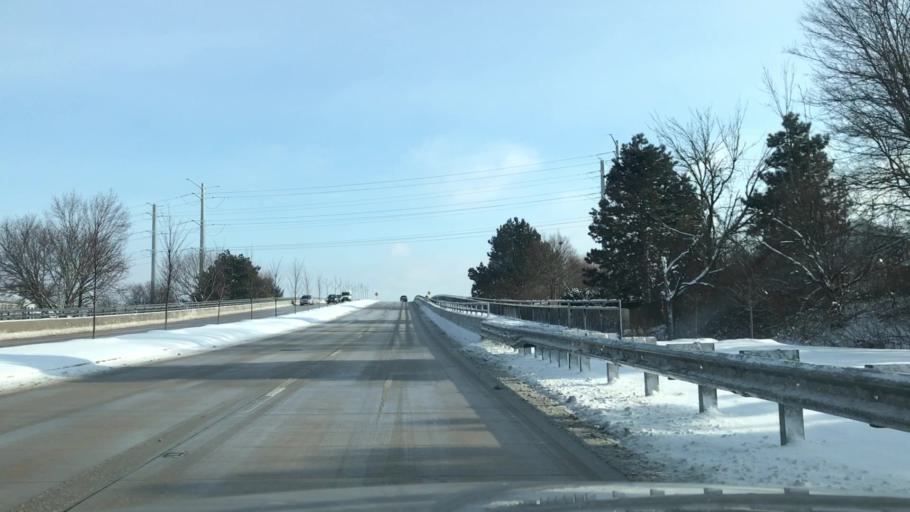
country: US
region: Illinois
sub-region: Kane County
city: Aurora
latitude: 41.7437
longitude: -88.2364
